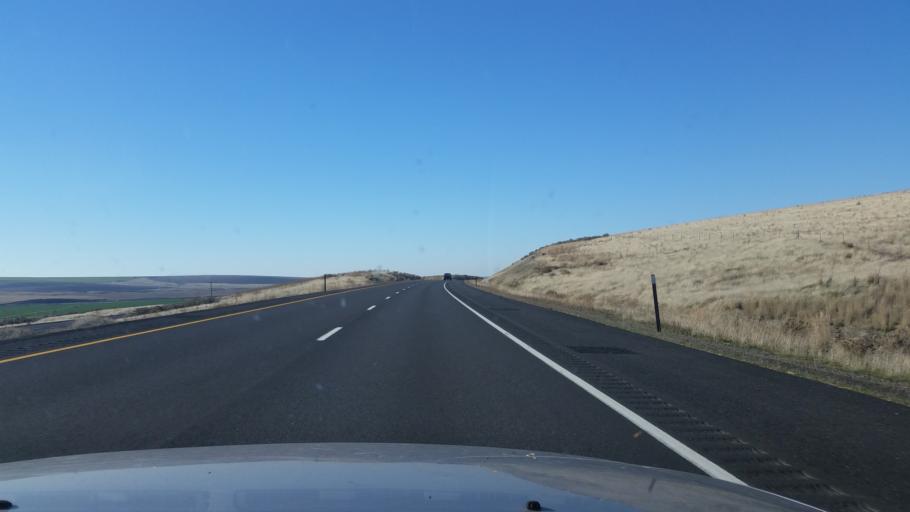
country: US
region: Washington
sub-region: Grant County
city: Warden
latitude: 47.0850
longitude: -118.9522
